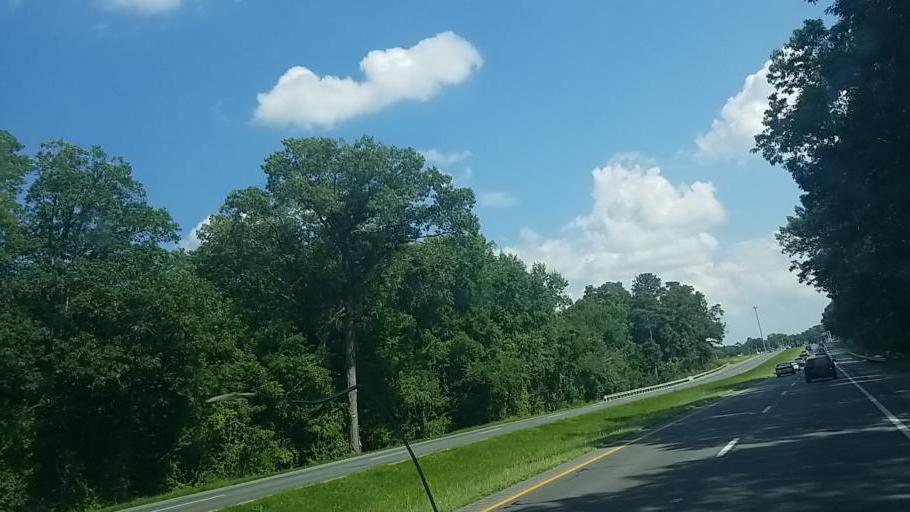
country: US
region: Delaware
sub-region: Sussex County
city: Millsboro
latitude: 38.6042
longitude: -75.3222
